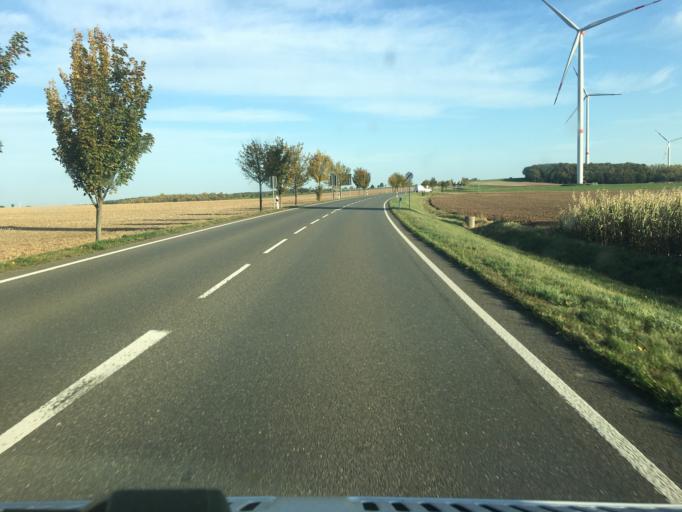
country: DE
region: Thuringia
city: Thonhausen
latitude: 50.8240
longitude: 12.3372
